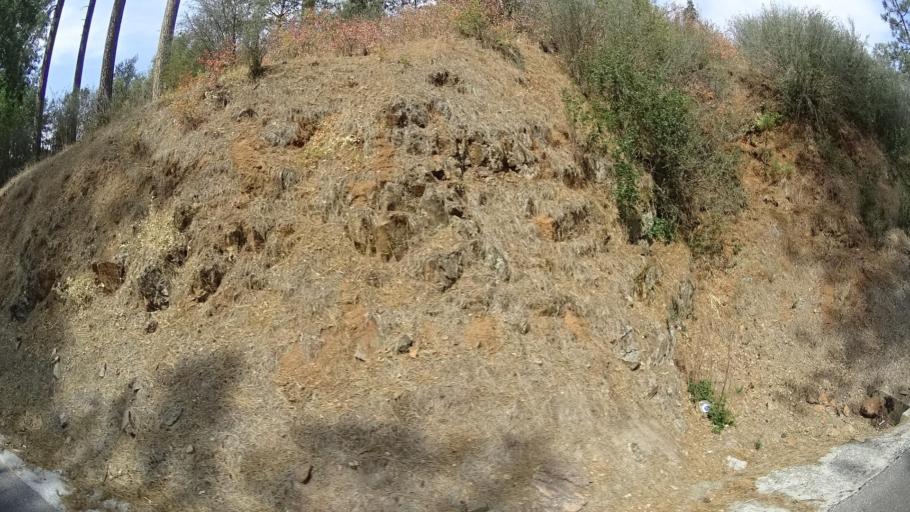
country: US
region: California
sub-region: Mariposa County
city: Midpines
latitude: 37.5291
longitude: -119.9181
